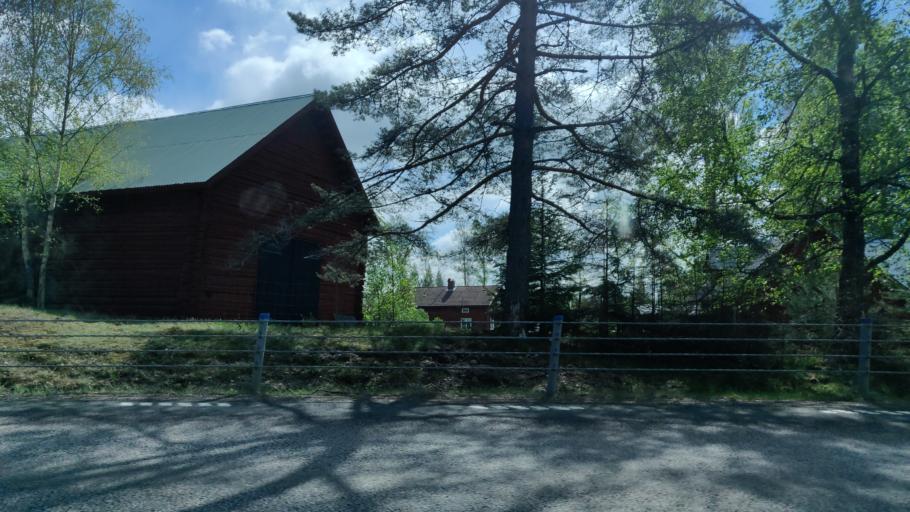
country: SE
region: Vaermland
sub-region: Karlstads Kommun
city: Molkom
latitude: 59.5461
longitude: 13.6465
